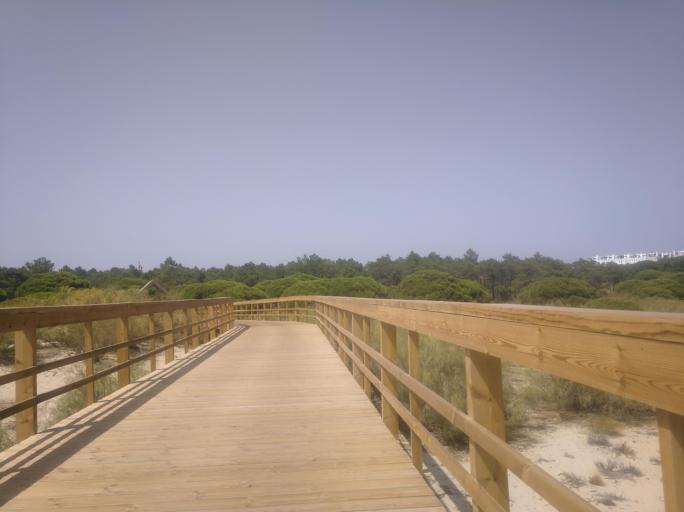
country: PT
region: Faro
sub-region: Vila Real de Santo Antonio
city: Monte Gordo
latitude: 37.1732
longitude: -7.4854
